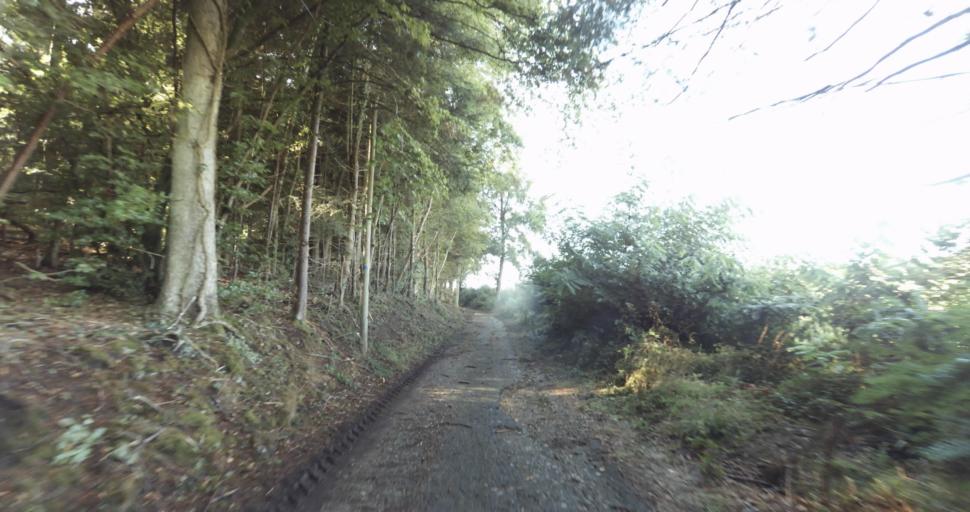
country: FR
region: Lower Normandy
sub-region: Departement de l'Orne
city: Vimoutiers
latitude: 48.9308
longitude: 0.2945
